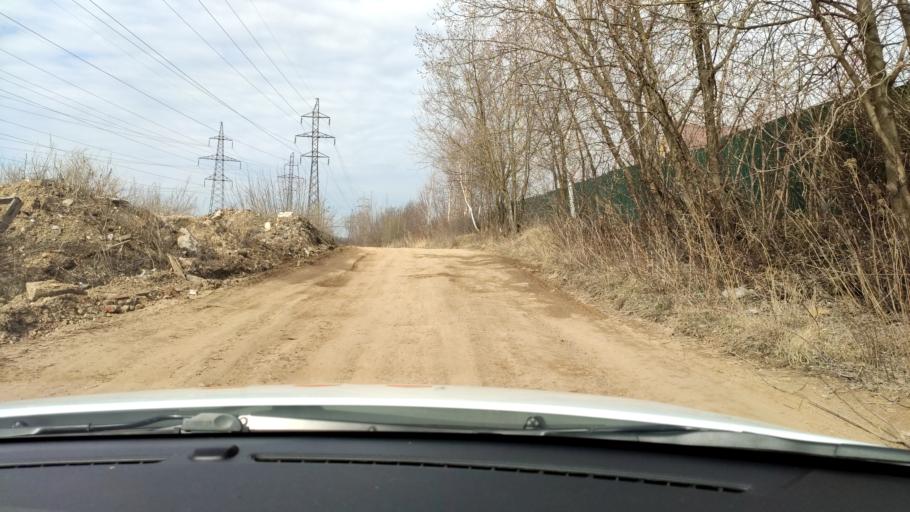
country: RU
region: Tatarstan
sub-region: Gorod Kazan'
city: Kazan
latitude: 55.8164
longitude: 49.2120
